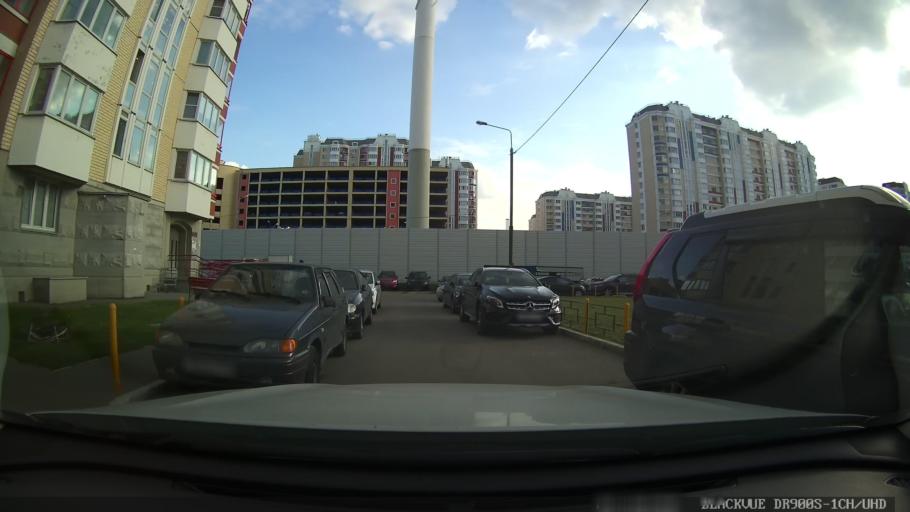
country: RU
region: Moskovskaya
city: Nemchinovka
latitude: 55.7265
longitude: 37.3569
